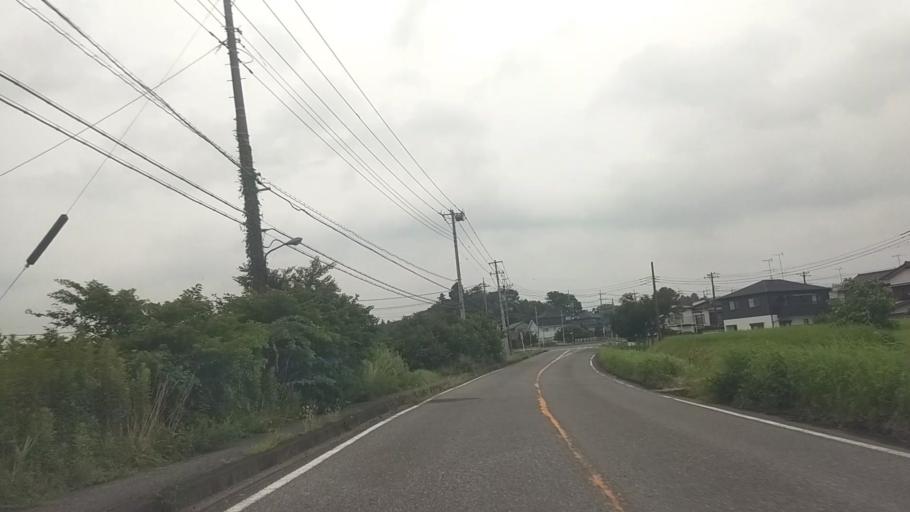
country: JP
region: Chiba
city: Kisarazu
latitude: 35.3884
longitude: 140.0470
